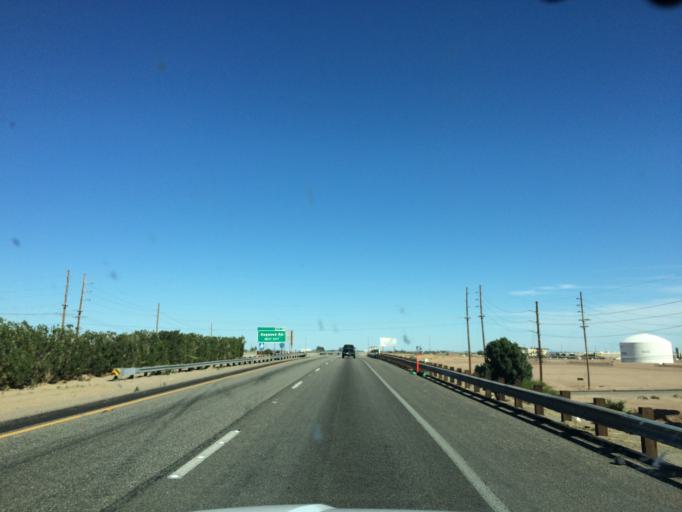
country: US
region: California
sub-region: Imperial County
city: El Centro
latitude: 32.7736
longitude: -115.5447
